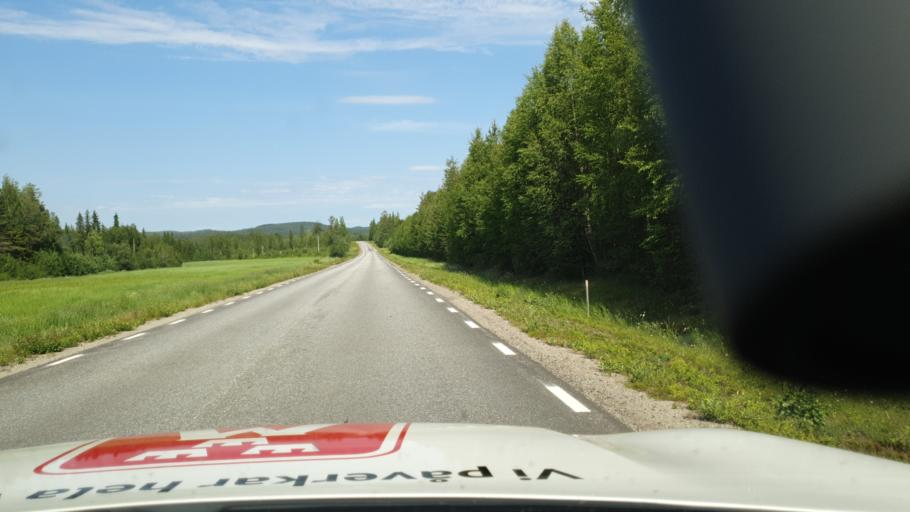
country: SE
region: Vaesterbotten
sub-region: Vindelns Kommun
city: Vindeln
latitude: 64.2130
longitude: 19.7645
